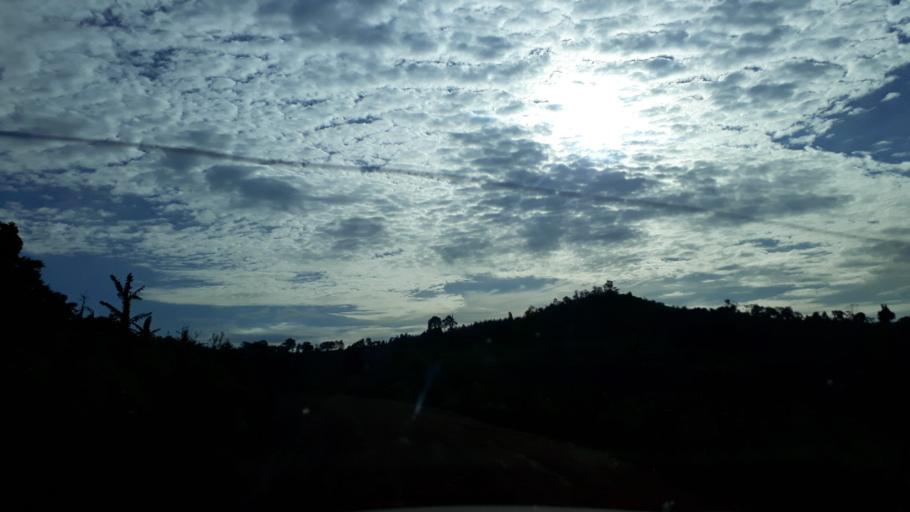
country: UG
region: Northern Region
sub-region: Zombo District
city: Paidha
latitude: 2.2556
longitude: 30.8732
